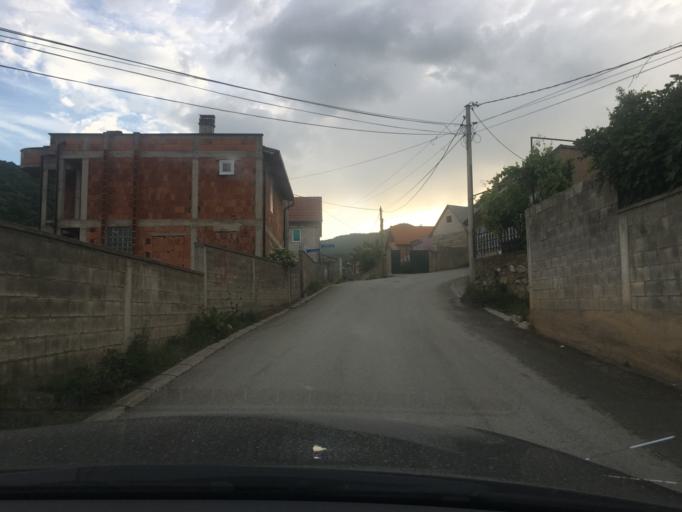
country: XK
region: Ferizaj
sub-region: Hani i Elezit
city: Hani i Elezit
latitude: 42.1449
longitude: 21.2909
